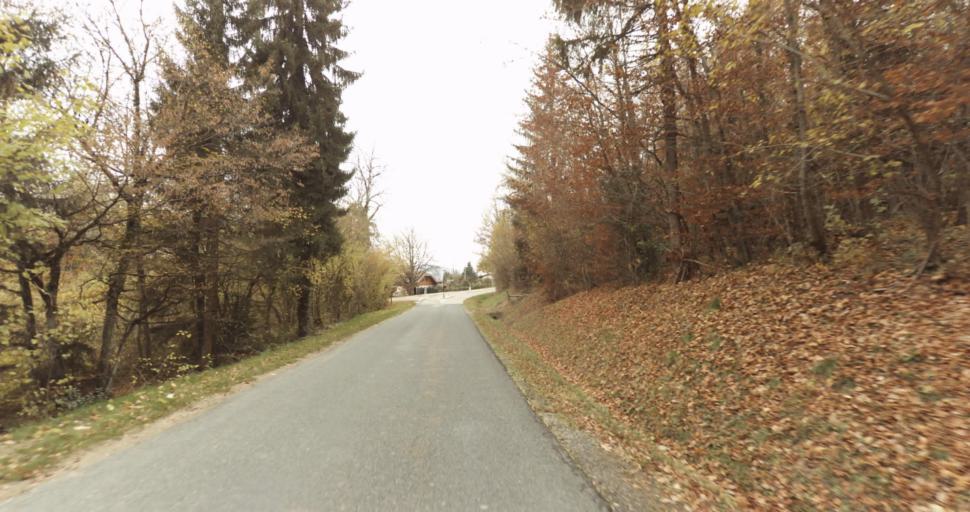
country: FR
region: Rhone-Alpes
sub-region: Departement de la Haute-Savoie
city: Saint-Martin-Bellevue
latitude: 45.9529
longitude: 6.1456
